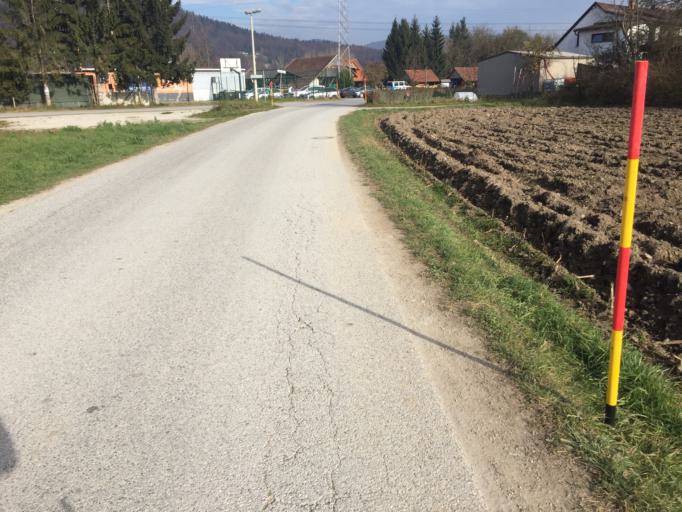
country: SI
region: Medvode
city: Zgornje Pirnice
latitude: 46.1153
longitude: 14.4554
